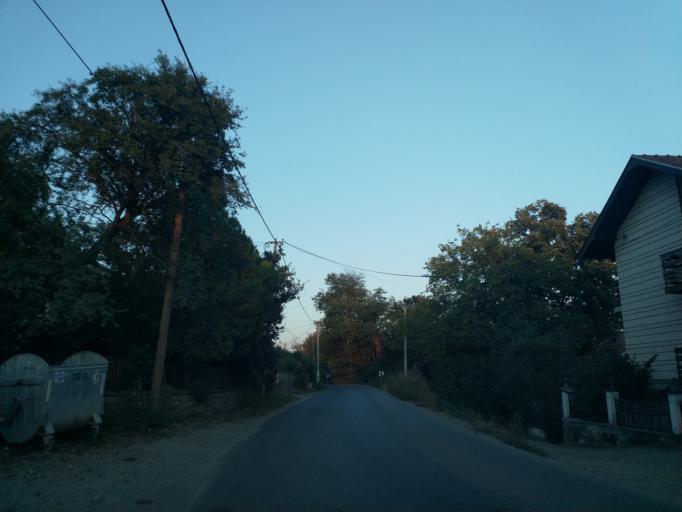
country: RS
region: Central Serbia
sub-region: Rasinski Okrug
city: Krusevac
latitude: 43.6028
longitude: 21.2235
